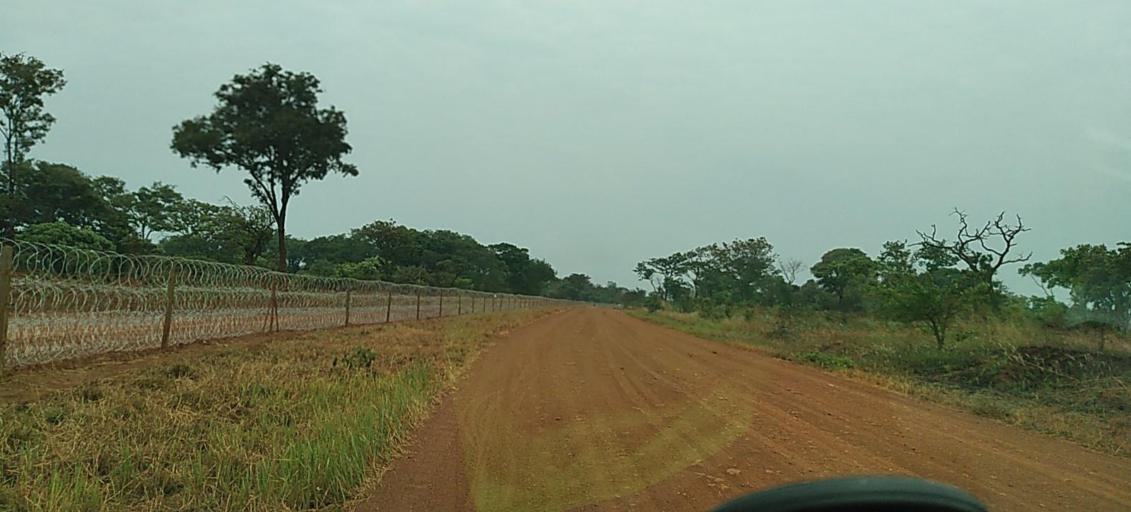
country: ZM
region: North-Western
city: Kansanshi
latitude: -12.0925
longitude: 26.4903
